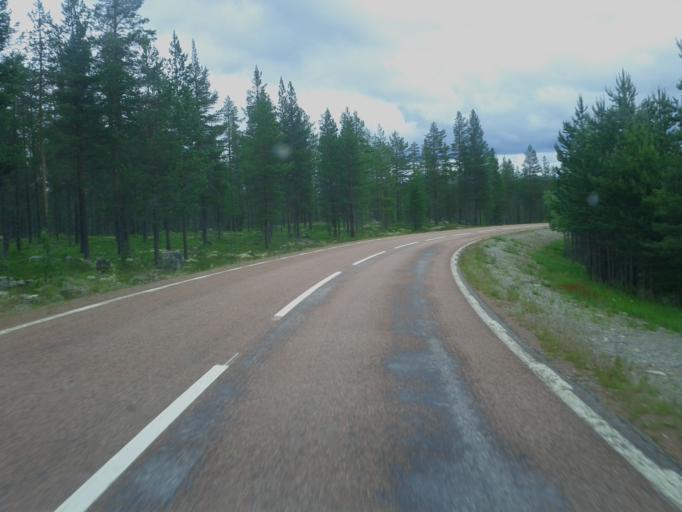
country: NO
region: Hedmark
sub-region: Engerdal
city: Engerdal
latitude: 61.8061
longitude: 12.4059
